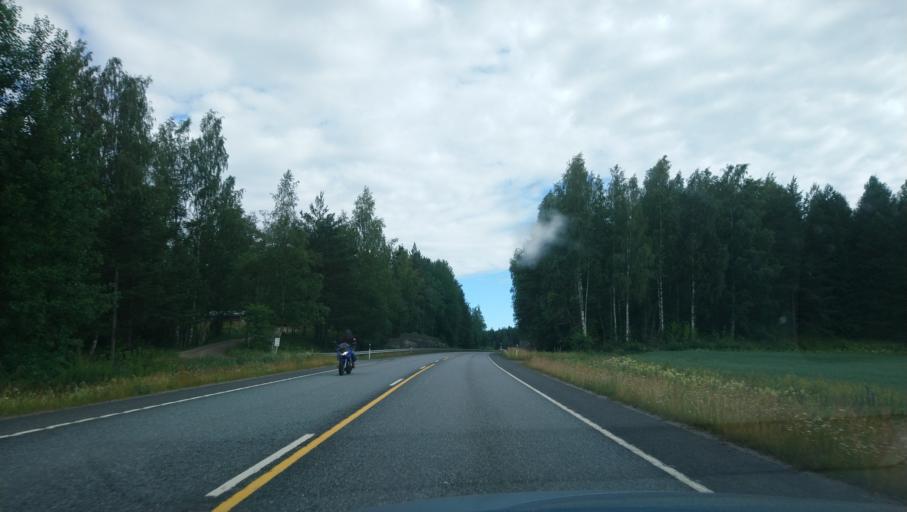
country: FI
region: Uusimaa
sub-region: Porvoo
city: Porvoo
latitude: 60.4181
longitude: 25.5793
